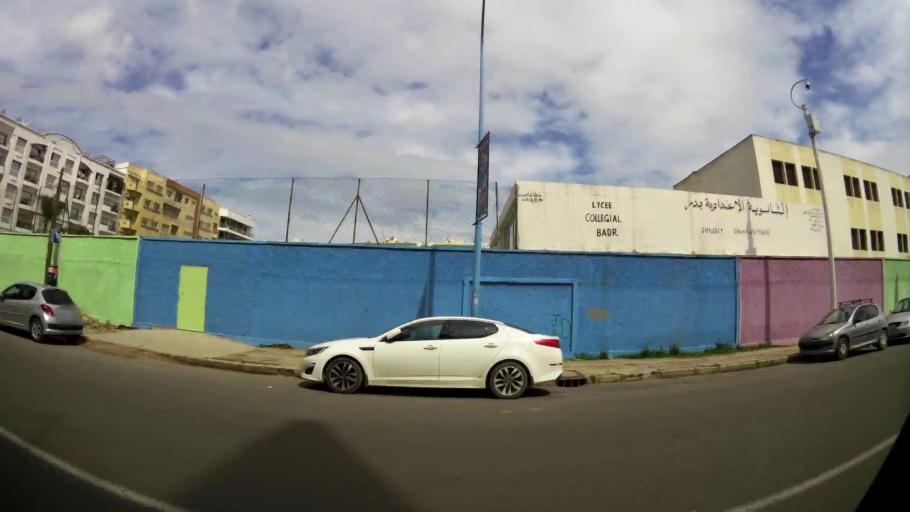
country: MA
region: Grand Casablanca
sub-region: Casablanca
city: Casablanca
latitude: 33.5855
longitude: -7.6420
